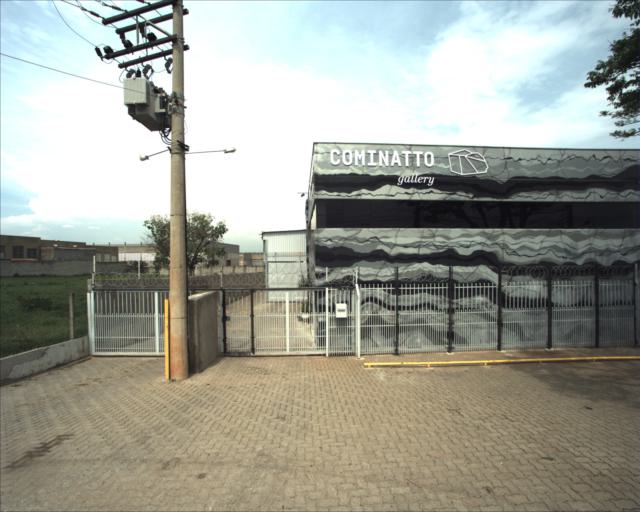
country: BR
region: Sao Paulo
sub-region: Sorocaba
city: Sorocaba
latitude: -23.4413
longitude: -47.4371
